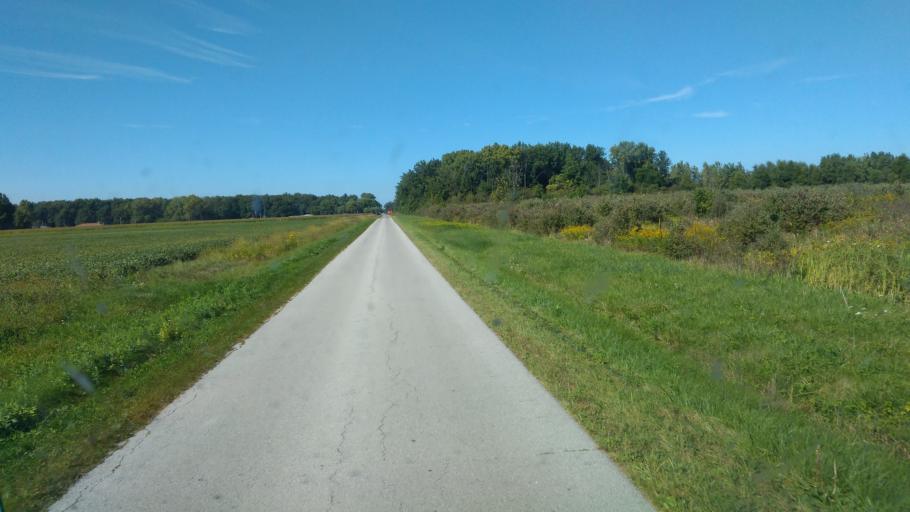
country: US
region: Ohio
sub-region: Sandusky County
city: Clyde
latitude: 41.4028
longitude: -82.9634
